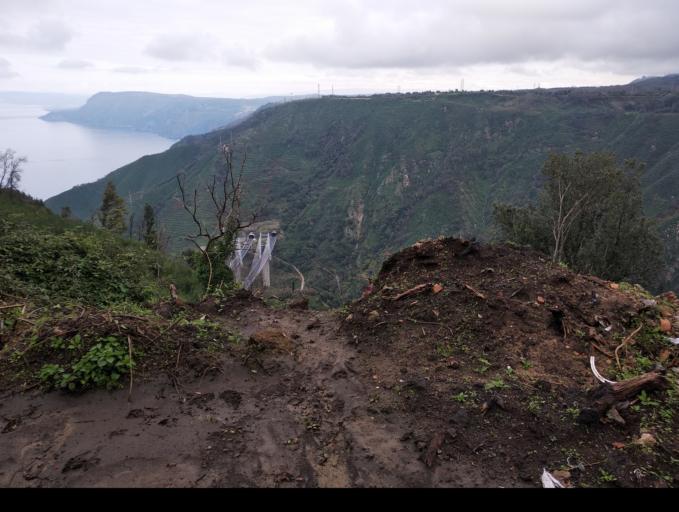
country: IT
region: Calabria
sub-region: Provincia di Reggio Calabria
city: Scilla
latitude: 38.2489
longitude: 15.7608
